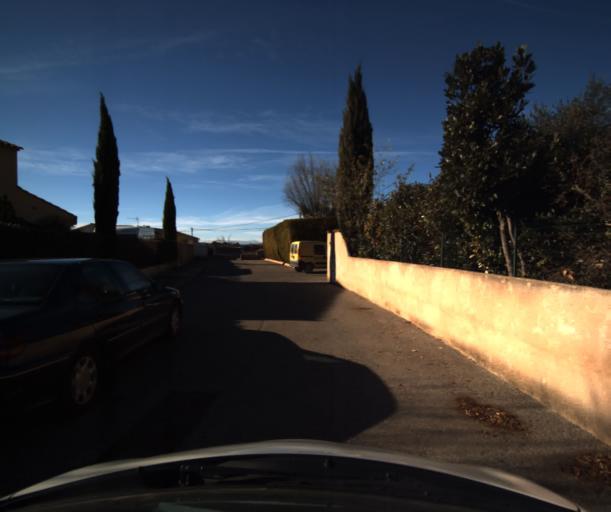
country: FR
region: Provence-Alpes-Cote d'Azur
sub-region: Departement du Vaucluse
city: Pertuis
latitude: 43.6997
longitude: 5.4787
